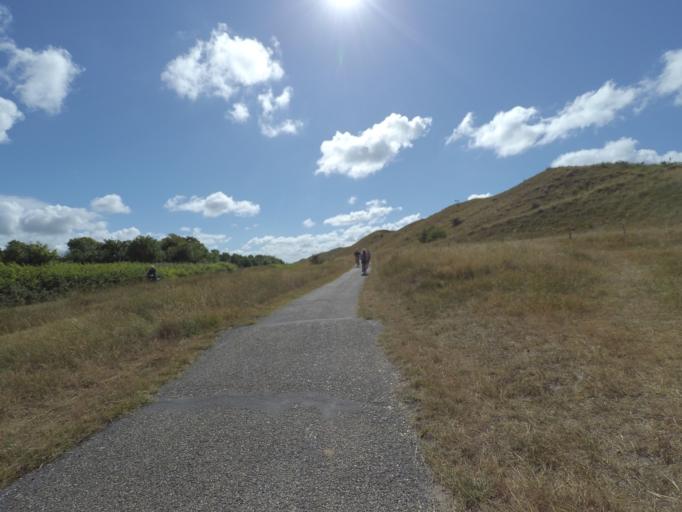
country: NL
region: North Holland
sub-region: Gemeente Texel
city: Den Burg
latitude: 53.1270
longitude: 4.8120
